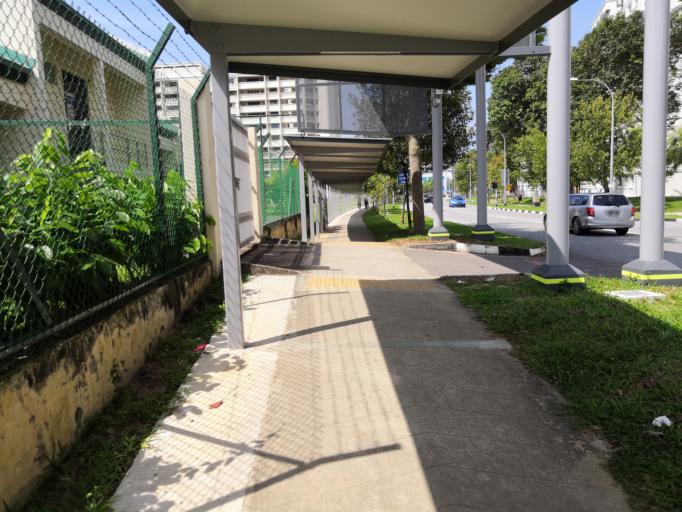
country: SG
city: Singapore
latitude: 1.3341
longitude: 103.9094
